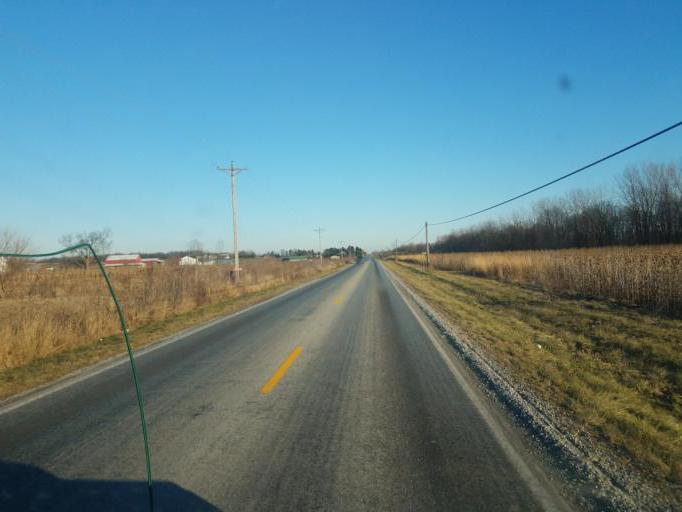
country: US
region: Ohio
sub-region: Hardin County
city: Kenton
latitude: 40.6241
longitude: -83.5261
